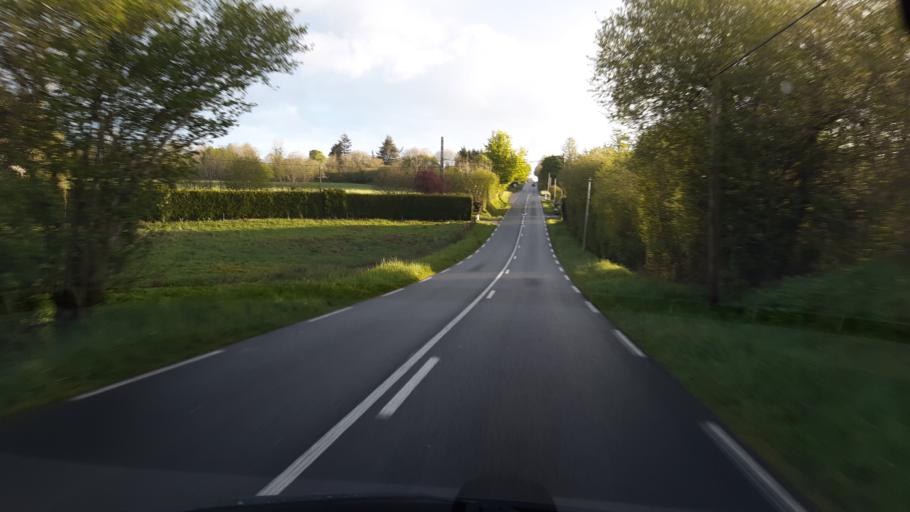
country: FR
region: Lower Normandy
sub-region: Departement de la Manche
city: Tessy-sur-Vire
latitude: 49.0208
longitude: -1.1469
